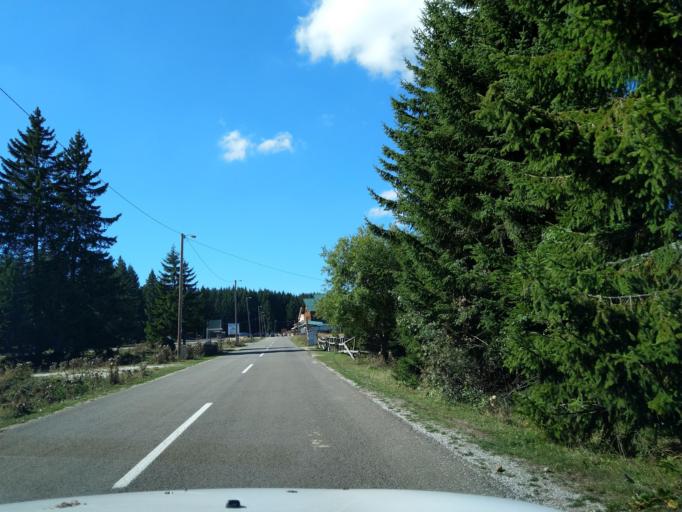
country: RS
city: Sokolovica
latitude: 43.2771
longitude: 20.3416
